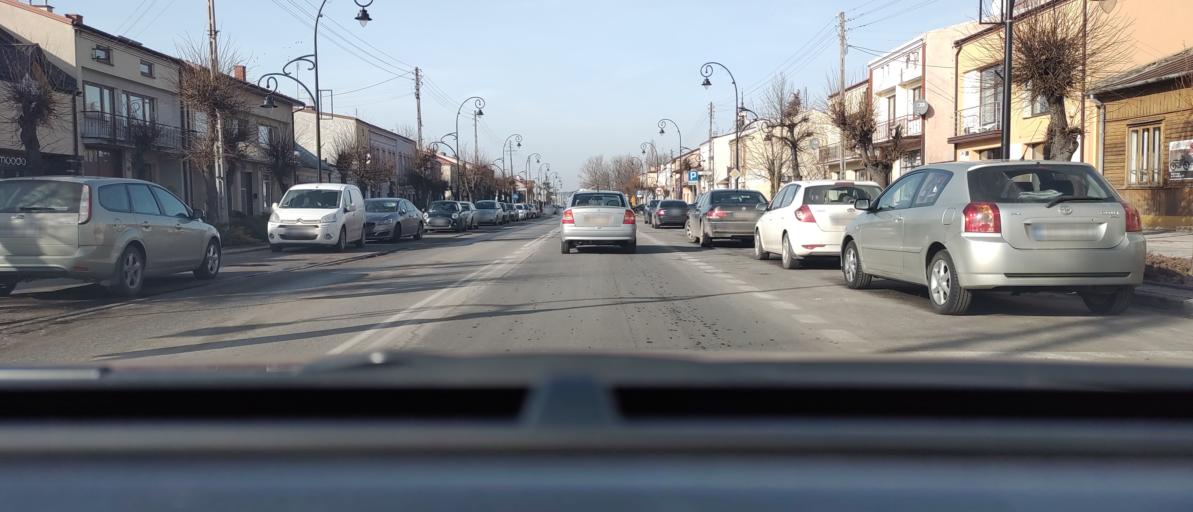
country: PL
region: Masovian Voivodeship
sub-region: Powiat bialobrzeski
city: Bialobrzegi
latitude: 51.6483
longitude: 20.9552
